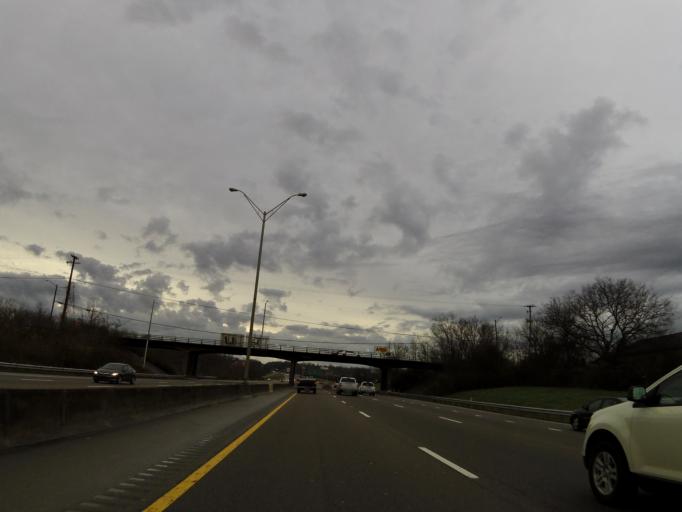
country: US
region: Tennessee
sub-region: Knox County
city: Knoxville
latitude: 36.0067
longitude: -83.9667
